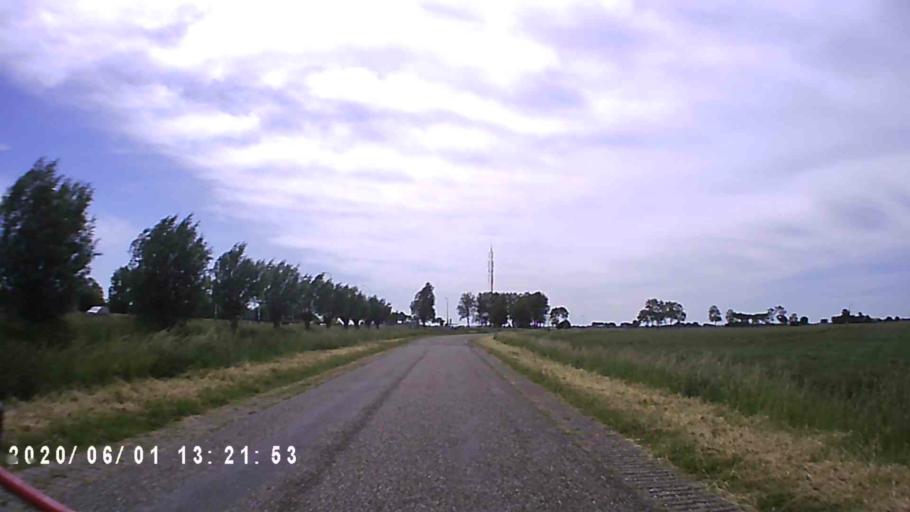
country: NL
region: Friesland
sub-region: Gemeente Littenseradiel
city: Wommels
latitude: 53.1102
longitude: 5.5824
